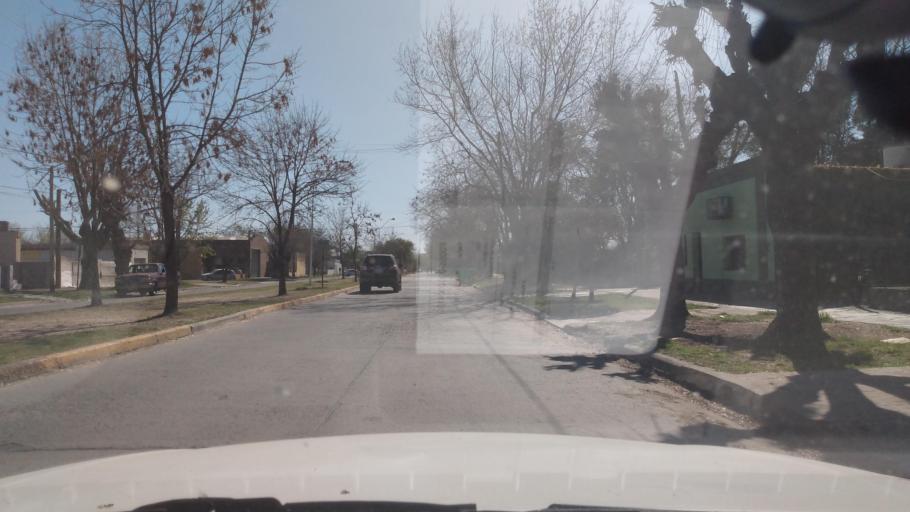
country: AR
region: Buenos Aires
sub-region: Partido de Mercedes
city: Mercedes
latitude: -34.6522
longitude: -59.4173
